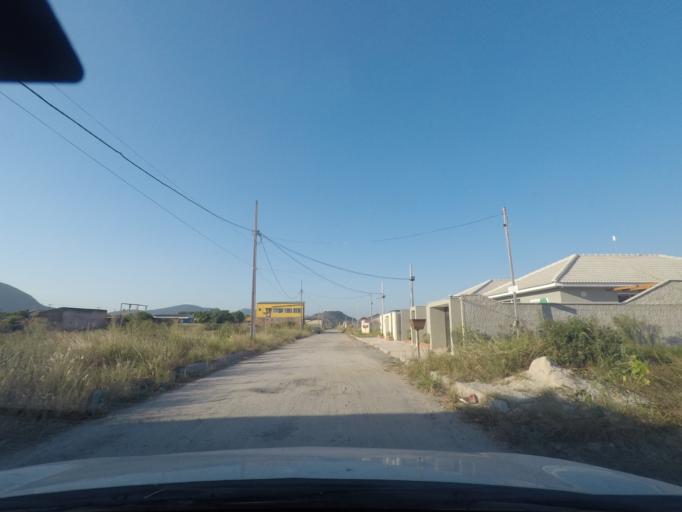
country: BR
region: Rio de Janeiro
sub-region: Marica
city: Marica
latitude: -22.9616
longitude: -42.9352
